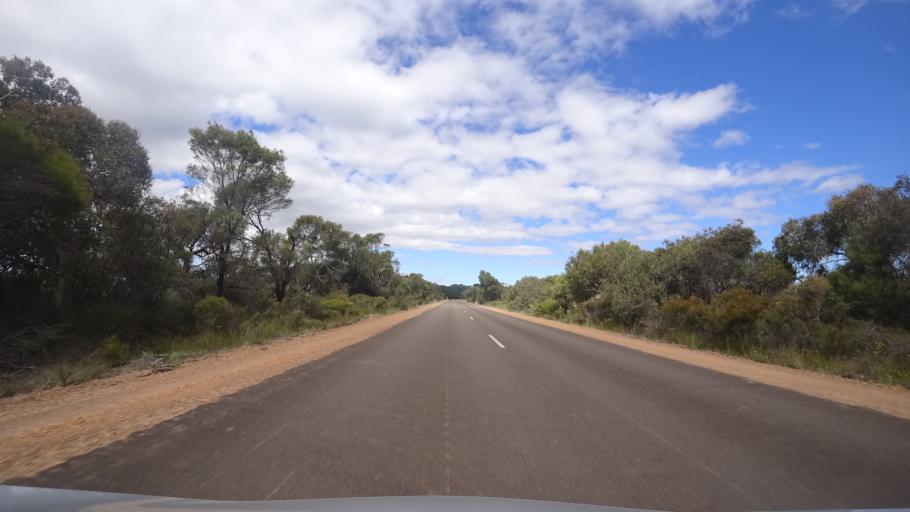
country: AU
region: South Australia
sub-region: Kangaroo Island
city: Kingscote
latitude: -35.7957
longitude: 137.0296
